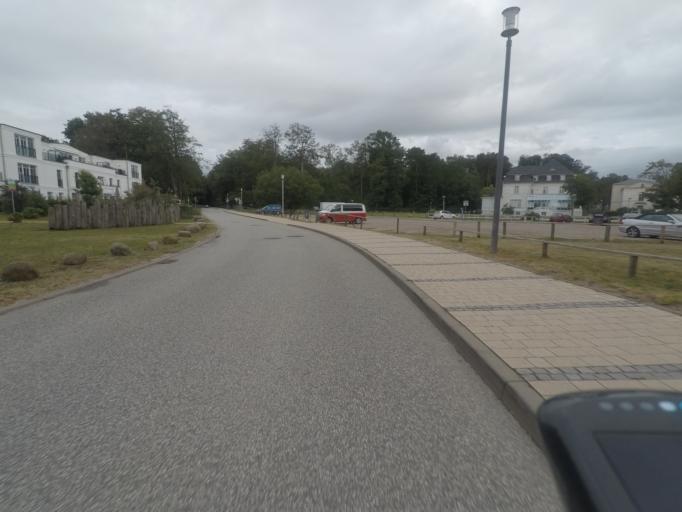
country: DE
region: Mecklenburg-Vorpommern
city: Bad Doberan
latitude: 54.1444
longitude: 11.8495
